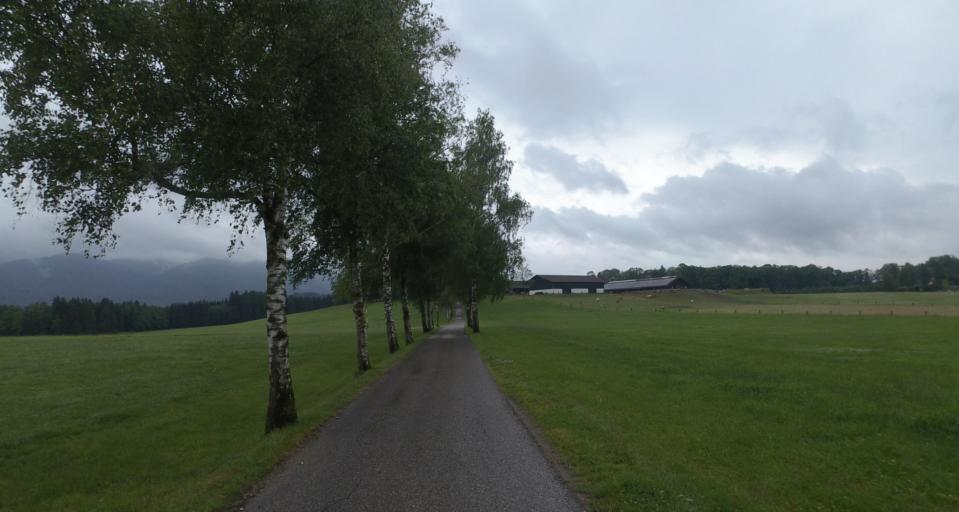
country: DE
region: Bavaria
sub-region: Upper Bavaria
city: Grabenstatt
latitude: 47.8223
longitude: 12.5268
